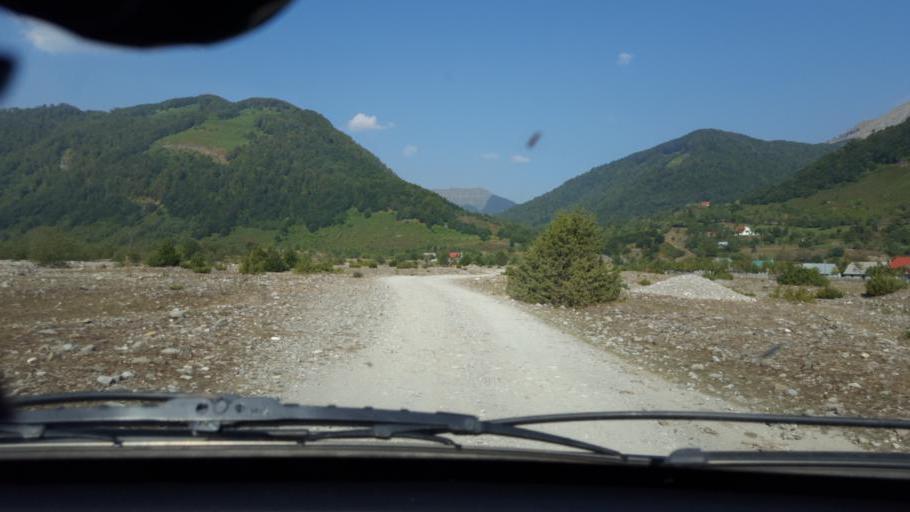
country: ME
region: Andrijevica
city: Andrijevica
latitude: 42.5977
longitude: 19.6644
